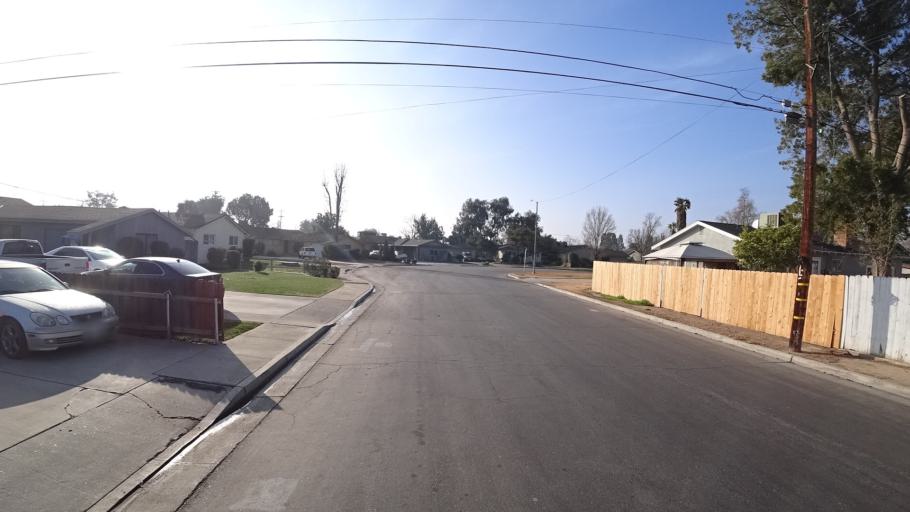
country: US
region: California
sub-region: Kern County
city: Bakersfield
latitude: 35.3358
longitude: -119.0261
